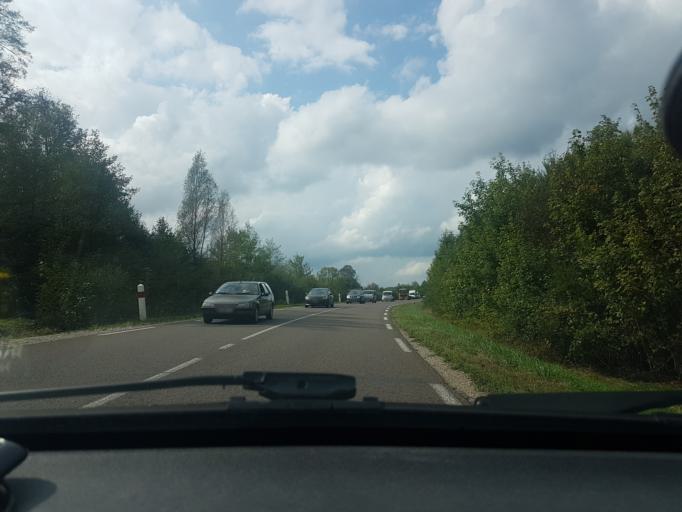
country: FR
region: Franche-Comte
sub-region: Departement du Doubs
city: Arcey
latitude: 47.5615
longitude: 6.6167
